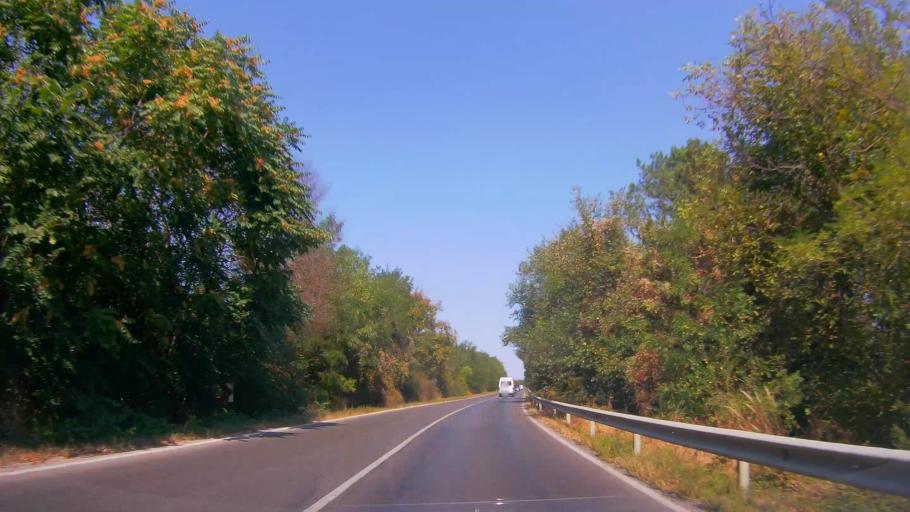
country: BG
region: Razgrad
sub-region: Obshtina Tsar Kaloyan
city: Tsar Kaloyan
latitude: 43.6225
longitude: 26.2117
